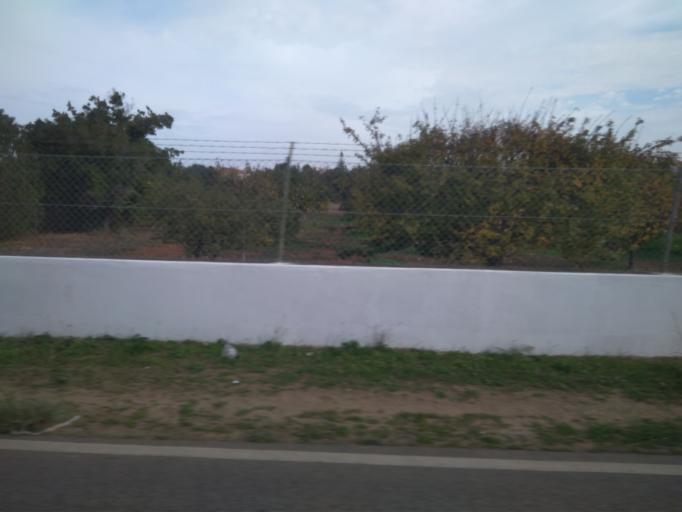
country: PT
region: Faro
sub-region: Faro
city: Santa Barbara de Nexe
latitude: 37.0772
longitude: -7.9597
